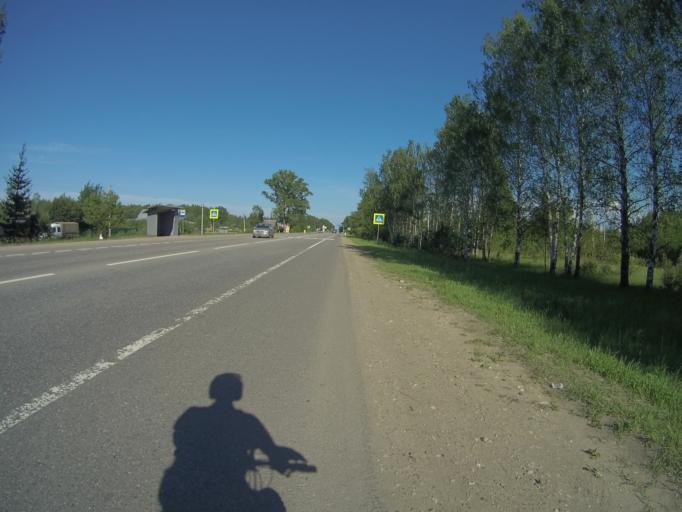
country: RU
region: Vladimir
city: Orgtrud
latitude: 56.2034
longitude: 40.7517
